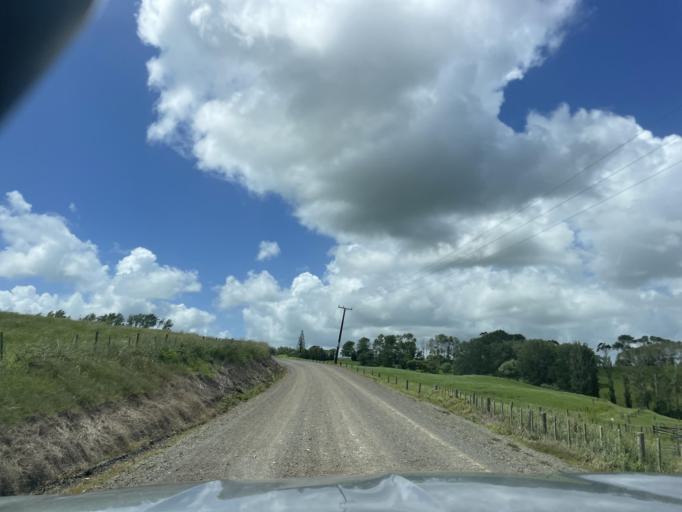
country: NZ
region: Auckland
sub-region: Auckland
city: Wellsford
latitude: -36.1721
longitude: 174.3178
